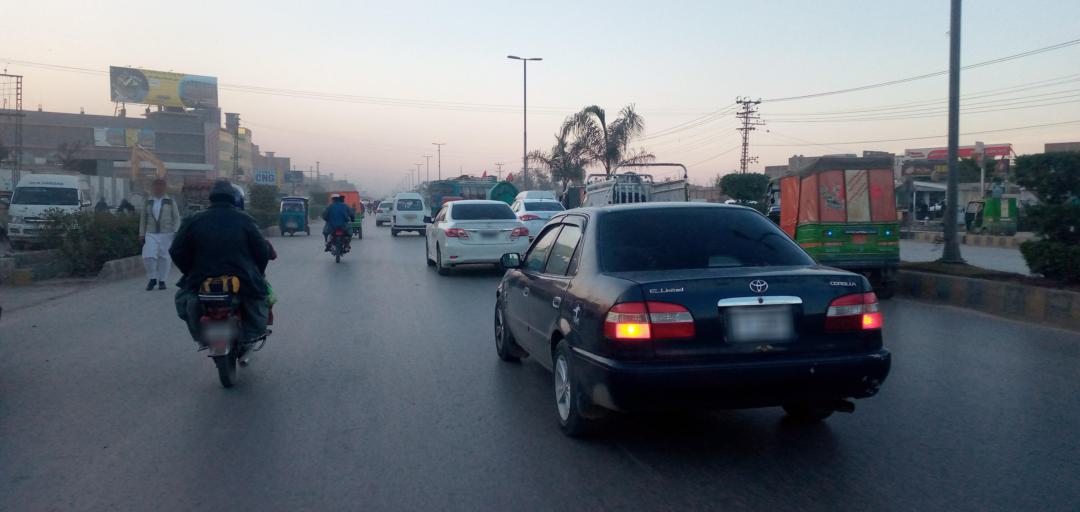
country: PK
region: Khyber Pakhtunkhwa
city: Peshawar
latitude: 34.0289
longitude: 71.6145
